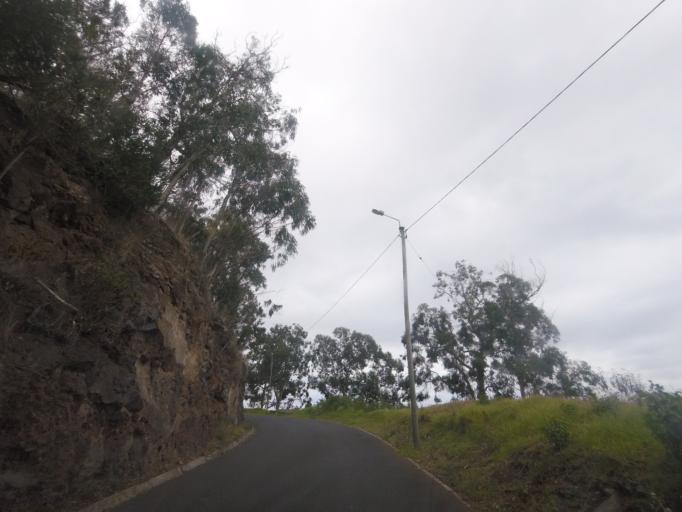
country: PT
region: Madeira
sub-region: Ribeira Brava
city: Campanario
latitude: 32.6581
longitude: -17.0063
